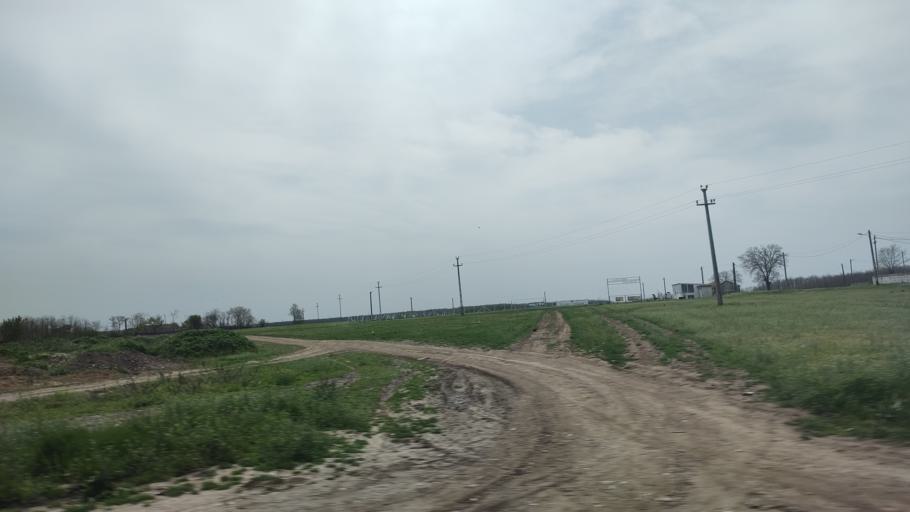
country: RO
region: Constanta
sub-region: Comuna Cobadin
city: Viisoara
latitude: 44.0776
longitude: 28.1813
